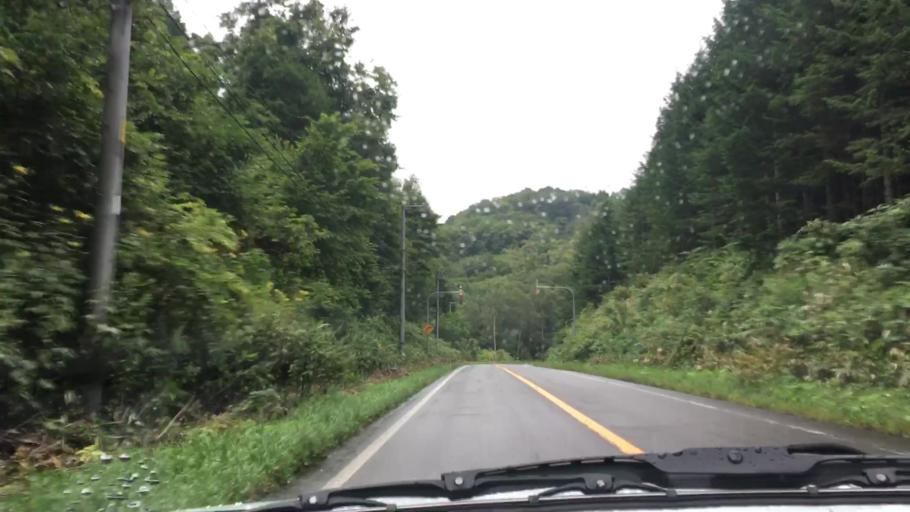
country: JP
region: Hokkaido
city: Niseko Town
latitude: 42.6159
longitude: 140.7287
